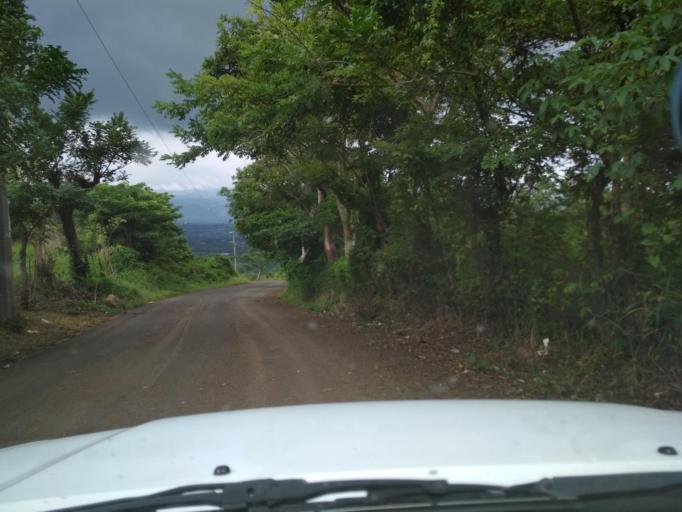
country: MX
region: Veracruz
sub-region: San Andres Tuxtla
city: El Huidero
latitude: 18.3827
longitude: -95.1773
